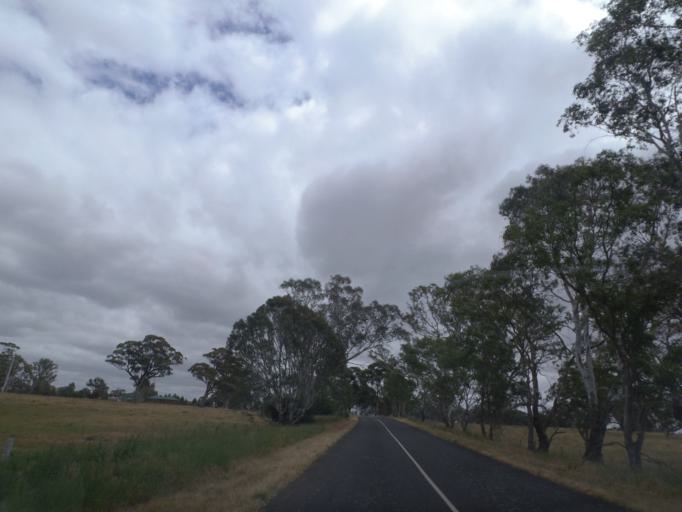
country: AU
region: Victoria
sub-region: Whittlesea
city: Whittlesea
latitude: -37.1089
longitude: 145.0240
